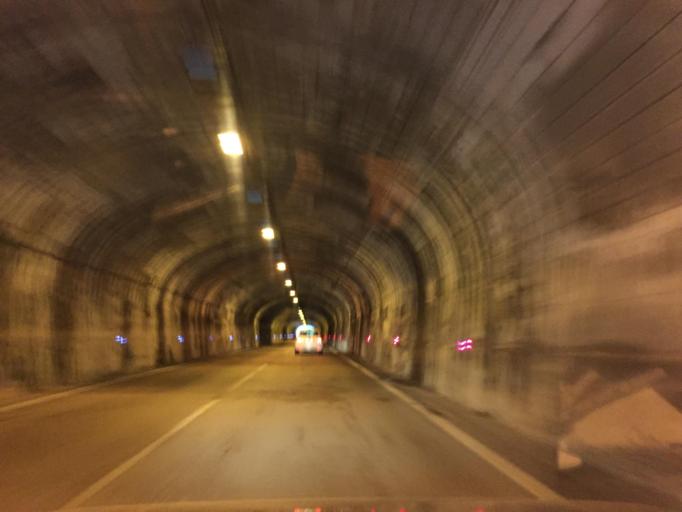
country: IT
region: Friuli Venezia Giulia
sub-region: Provincia di Pordenone
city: Montereale Valcellina
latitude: 46.1647
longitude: 12.6531
